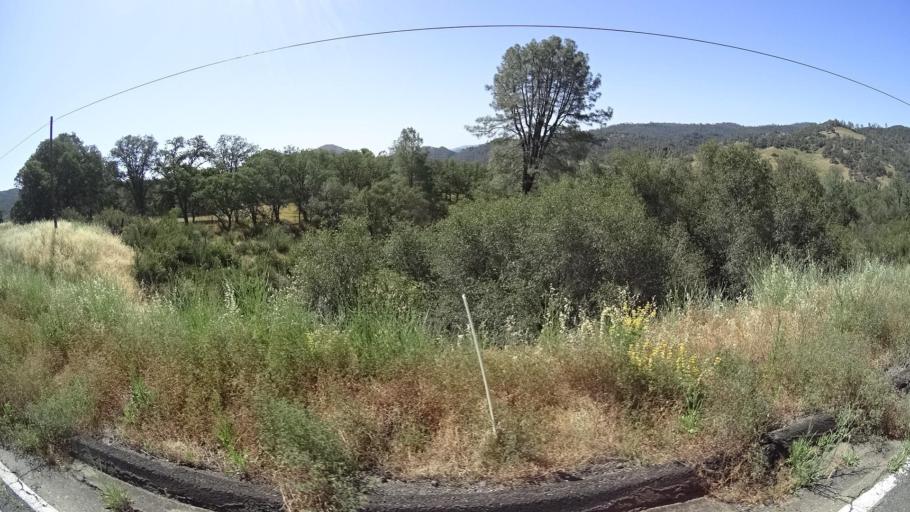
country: US
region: California
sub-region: Lake County
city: Hidden Valley Lake
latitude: 38.8782
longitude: -122.5275
